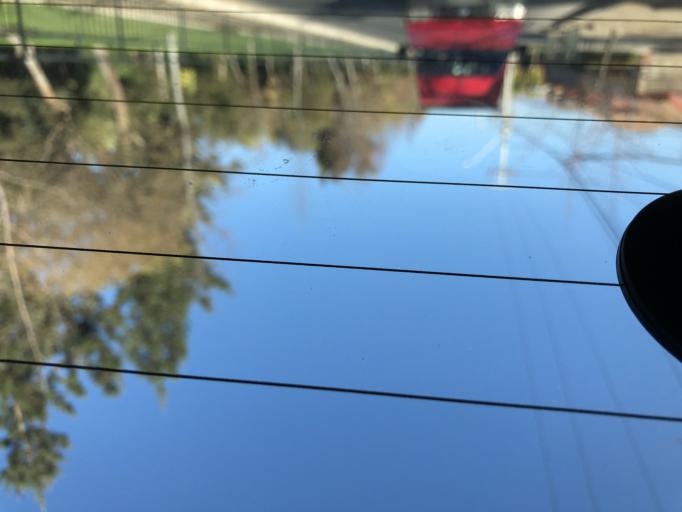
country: CL
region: Santiago Metropolitan
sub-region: Provincia de Cordillera
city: Puente Alto
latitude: -33.5546
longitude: -70.5530
